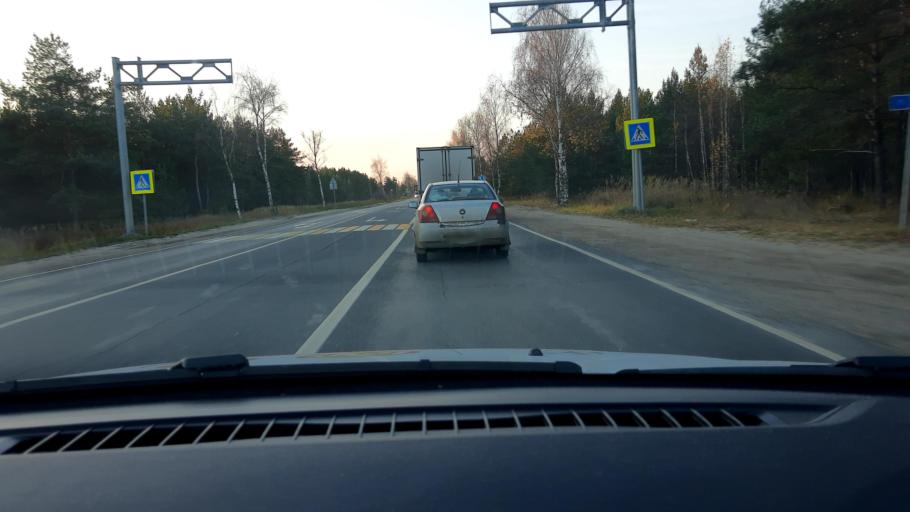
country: RU
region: Nizjnij Novgorod
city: Dzerzhinsk
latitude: 56.2888
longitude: 43.4757
